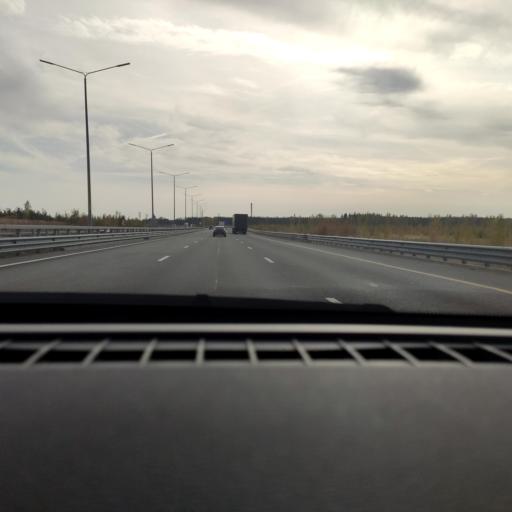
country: RU
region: Voronezj
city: Somovo
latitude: 51.7530
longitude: 39.3063
